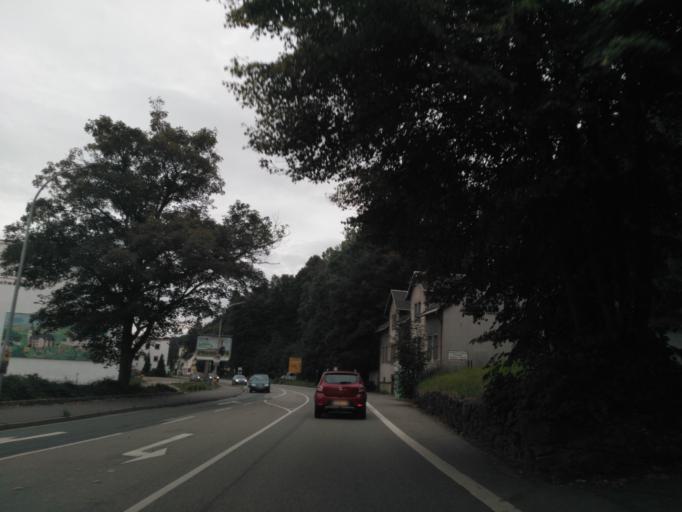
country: DE
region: Saxony
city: Schwarzenberg
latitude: 50.5418
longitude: 12.7931
